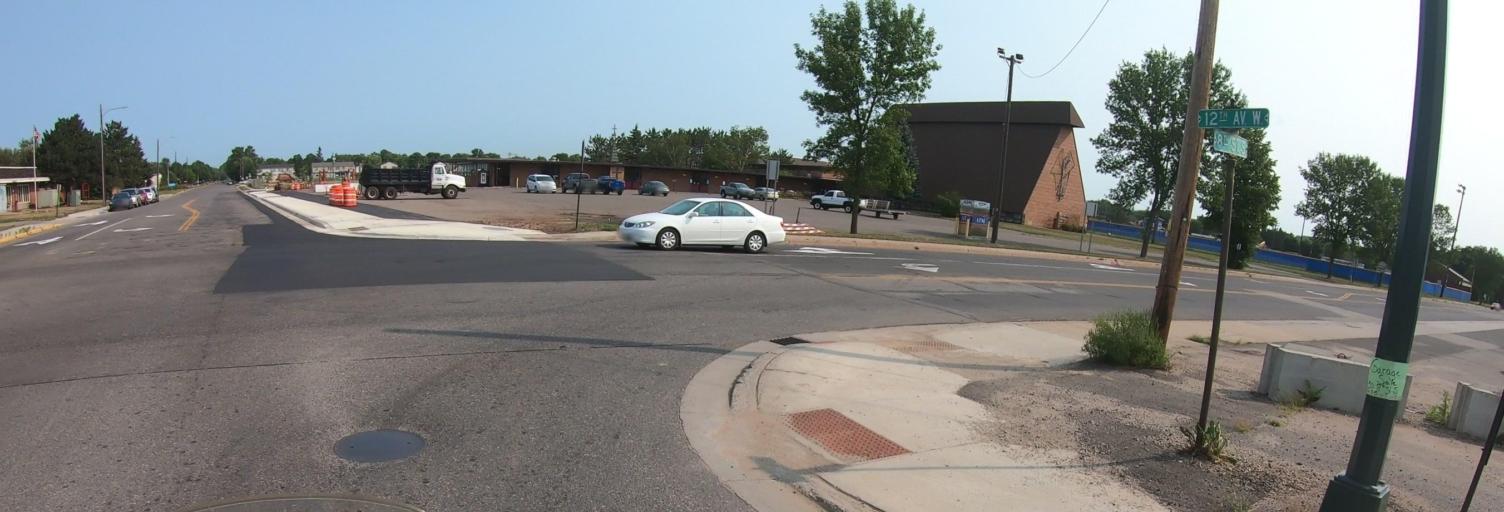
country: US
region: Minnesota
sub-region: Saint Louis County
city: Virginia
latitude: 47.5157
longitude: -92.5516
